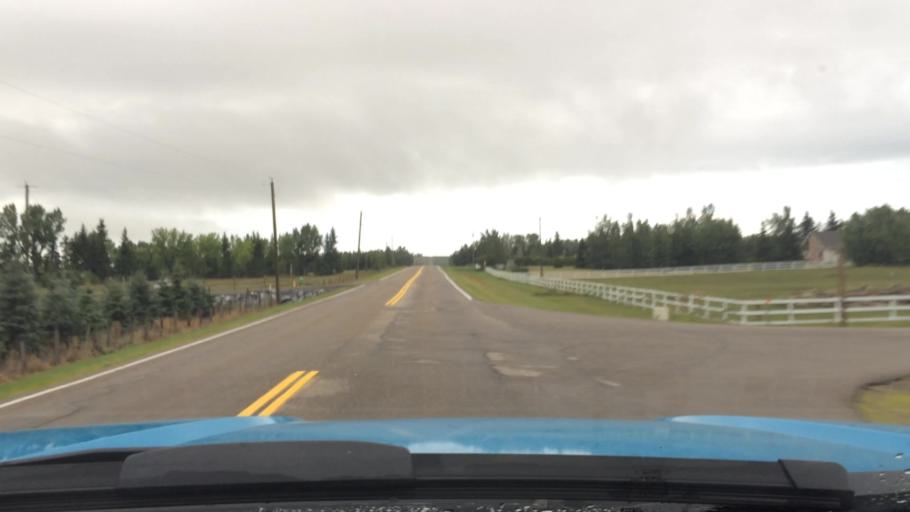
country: CA
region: Alberta
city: Airdrie
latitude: 51.2008
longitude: -114.1412
